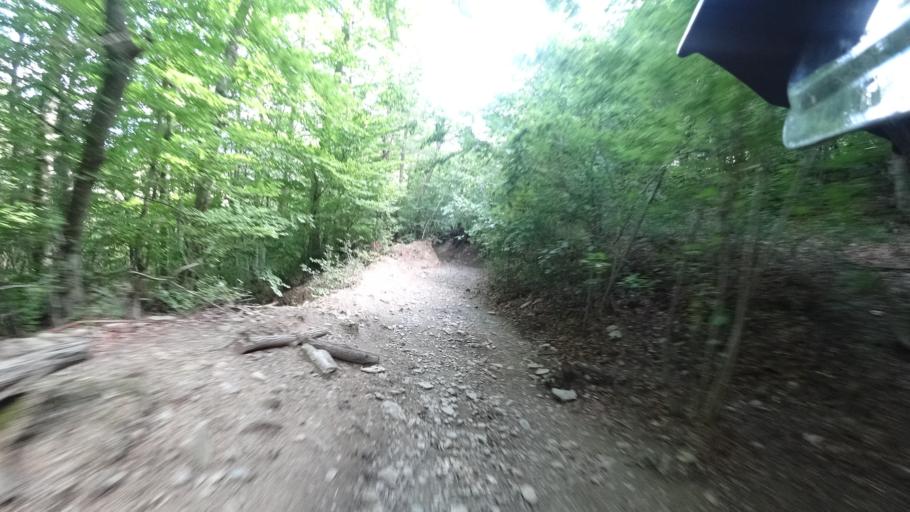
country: HR
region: Zadarska
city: Gracac
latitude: 44.3654
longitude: 16.0873
